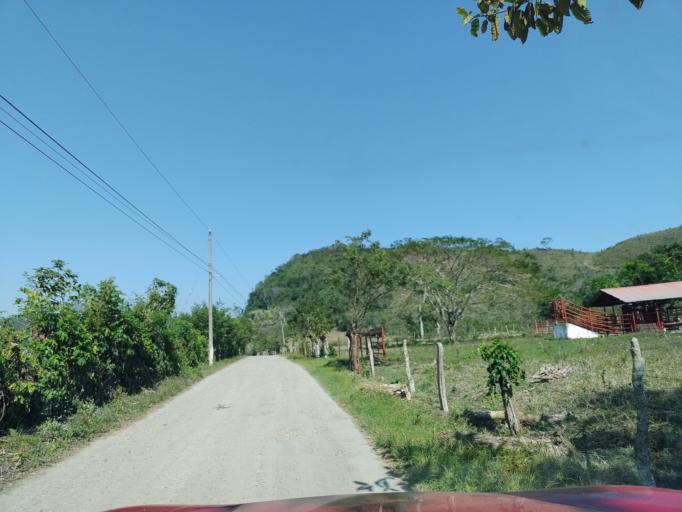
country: MX
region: Veracruz
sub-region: Papantla
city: Polutla
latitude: 20.4859
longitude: -97.1895
